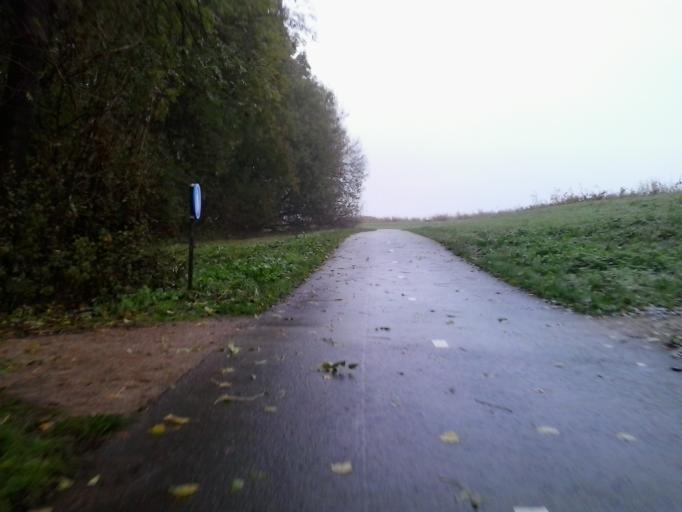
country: NL
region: South Holland
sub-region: Gemeente Lansingerland
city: Bleiswijk
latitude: 51.9950
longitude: 4.5470
